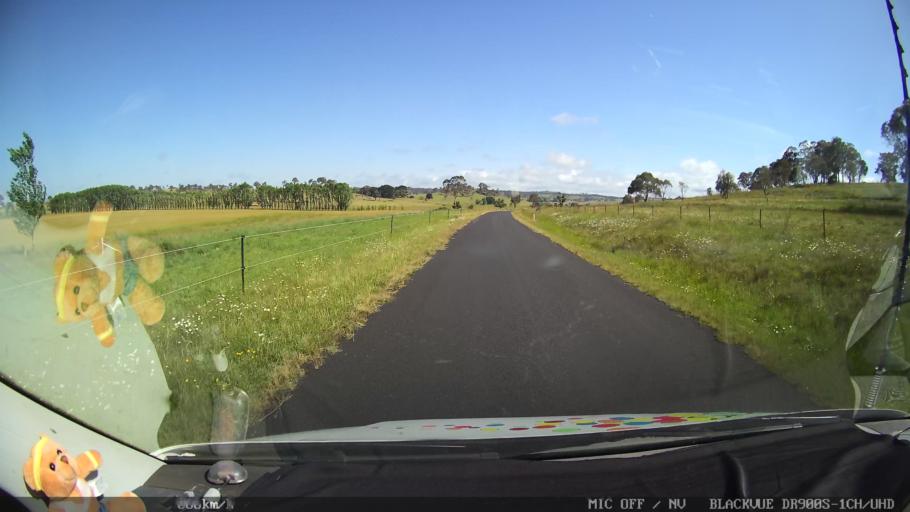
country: AU
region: New South Wales
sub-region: Guyra
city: Guyra
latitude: -30.1561
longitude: 151.6809
